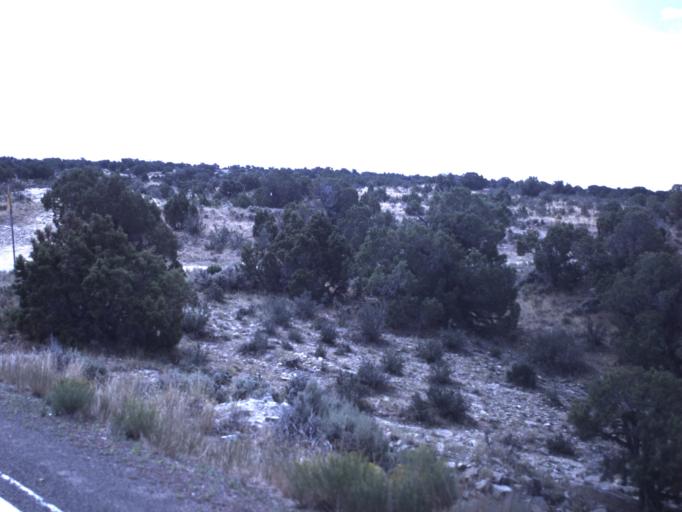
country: US
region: Utah
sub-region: Daggett County
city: Manila
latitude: 40.9392
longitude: -109.7127
